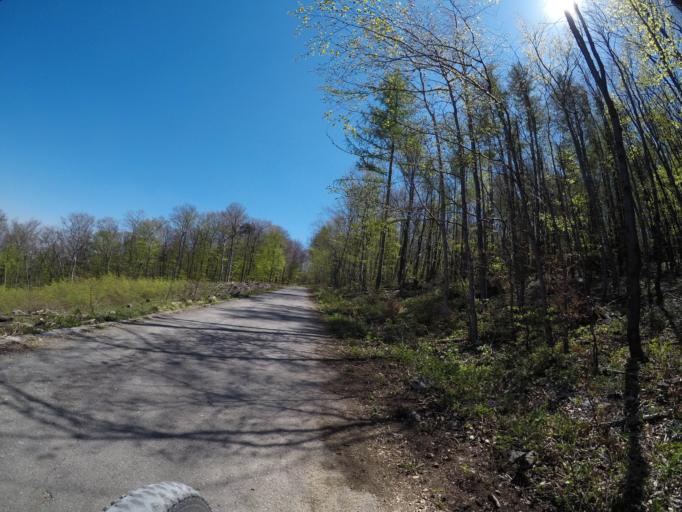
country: AT
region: Lower Austria
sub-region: Politischer Bezirk Modling
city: Gumpoldskirchen
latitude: 48.0532
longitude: 16.2485
